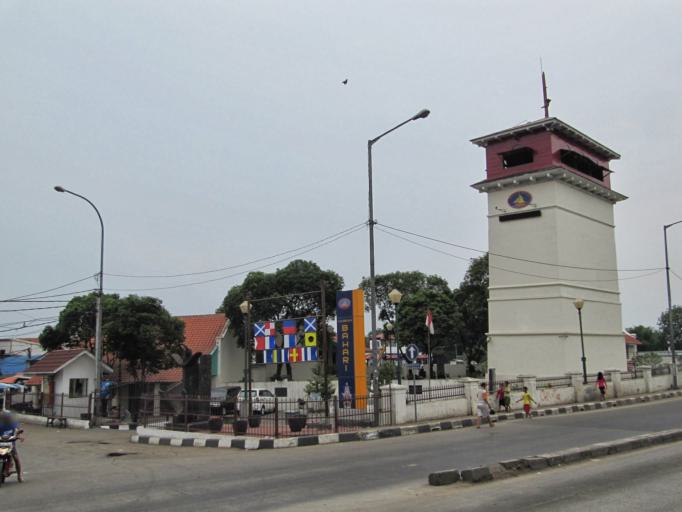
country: ID
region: Jakarta Raya
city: Jakarta
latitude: -6.1277
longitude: 106.8088
